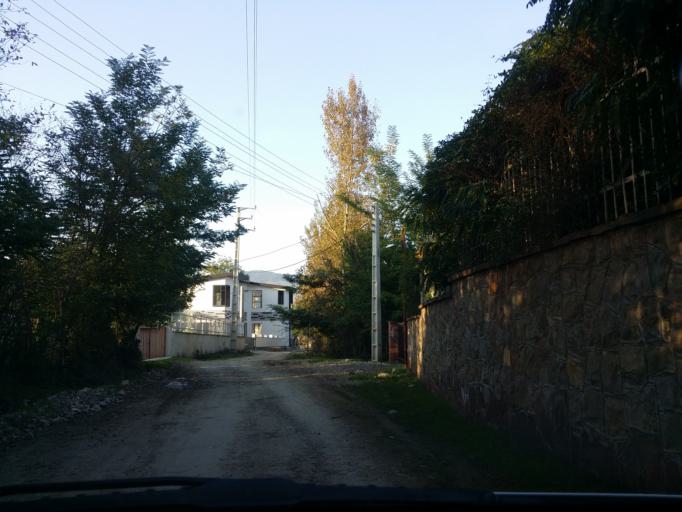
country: IR
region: Mazandaran
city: `Abbasabad
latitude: 36.5126
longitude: 51.1900
